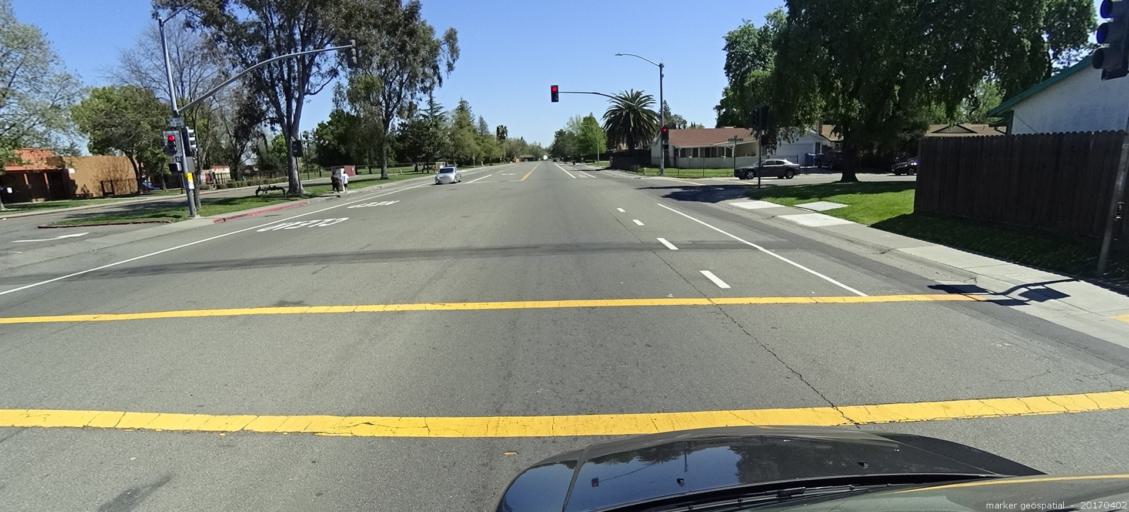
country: US
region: California
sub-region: Sacramento County
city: Parkway
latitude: 38.4659
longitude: -121.4402
